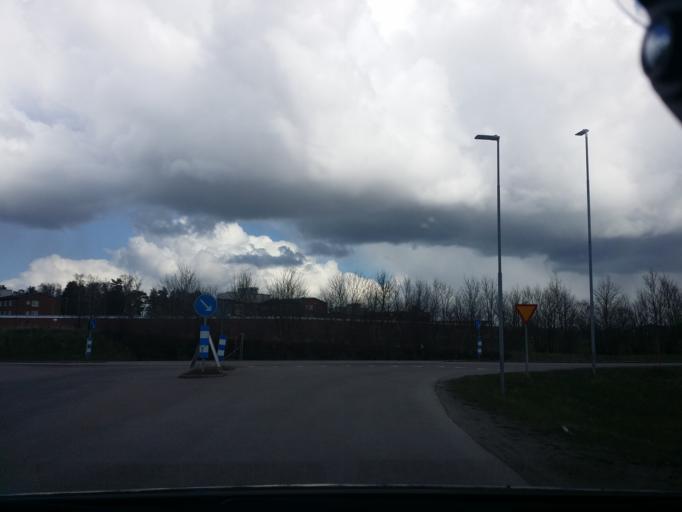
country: SE
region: Vaestmanland
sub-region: Sala Kommun
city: Sala
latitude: 59.9236
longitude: 16.5786
